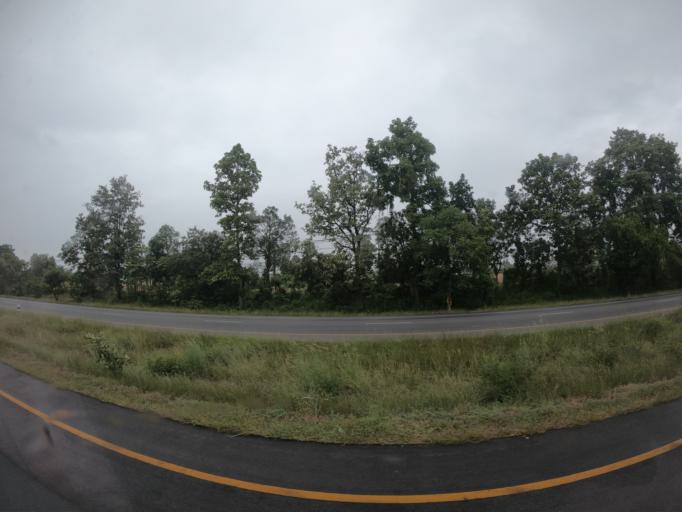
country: TH
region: Maha Sarakham
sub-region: Amphoe Borabue
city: Borabue
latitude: 16.0578
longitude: 103.0611
